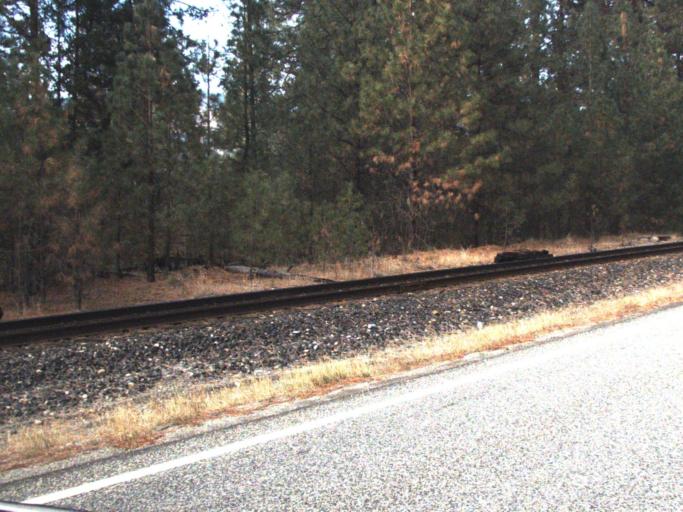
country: US
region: Washington
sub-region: Stevens County
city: Kettle Falls
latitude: 48.7821
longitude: -118.0026
